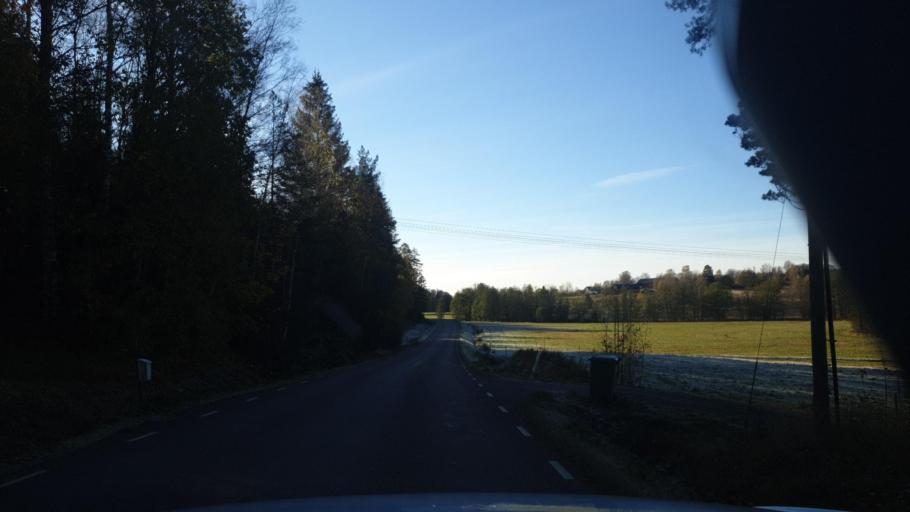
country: SE
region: Vaermland
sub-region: Grums Kommun
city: Grums
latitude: 59.4046
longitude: 13.0712
